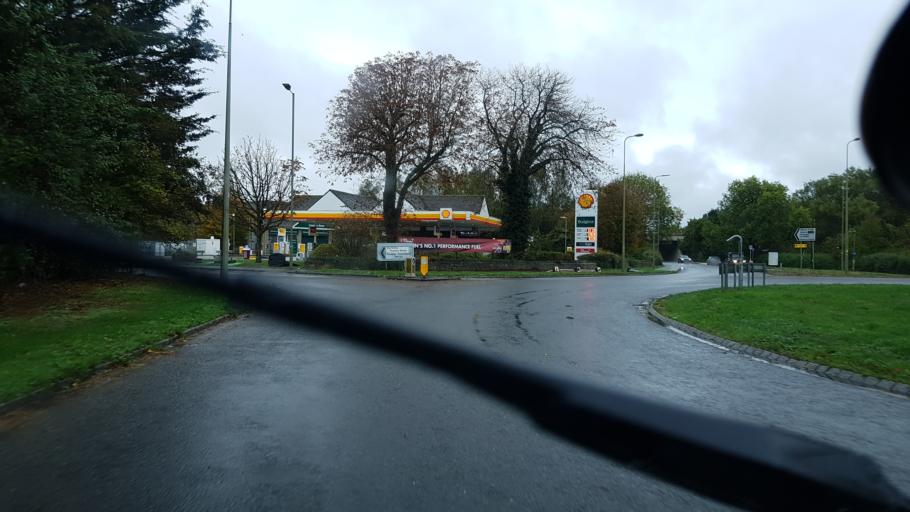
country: GB
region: England
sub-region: Oxfordshire
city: Ducklington
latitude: 51.7734
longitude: -1.4922
